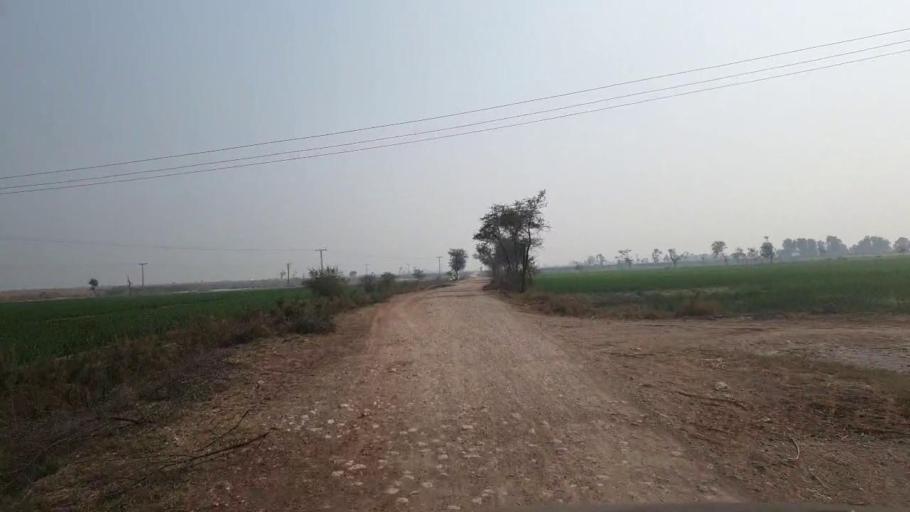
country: PK
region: Sindh
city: Hala
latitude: 25.9318
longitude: 68.4721
